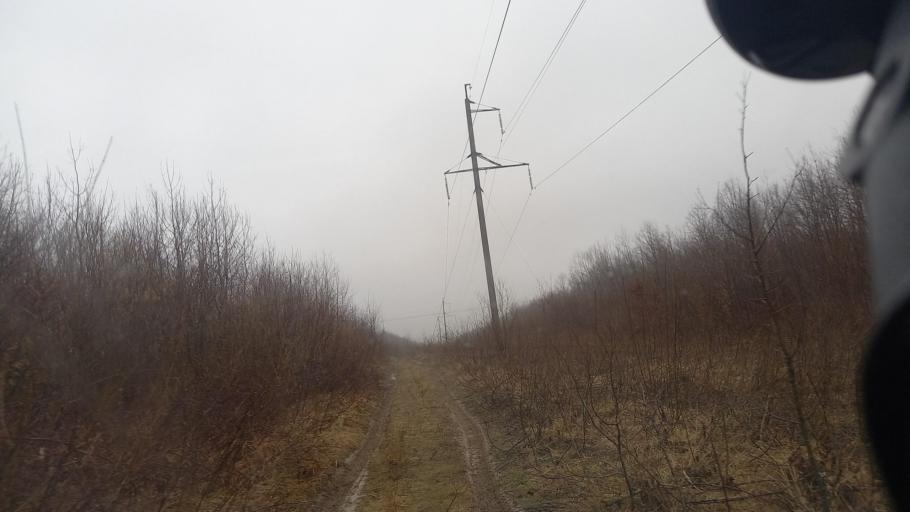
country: RU
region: Krasnodarskiy
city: Saratovskaya
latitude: 44.6318
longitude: 39.2579
